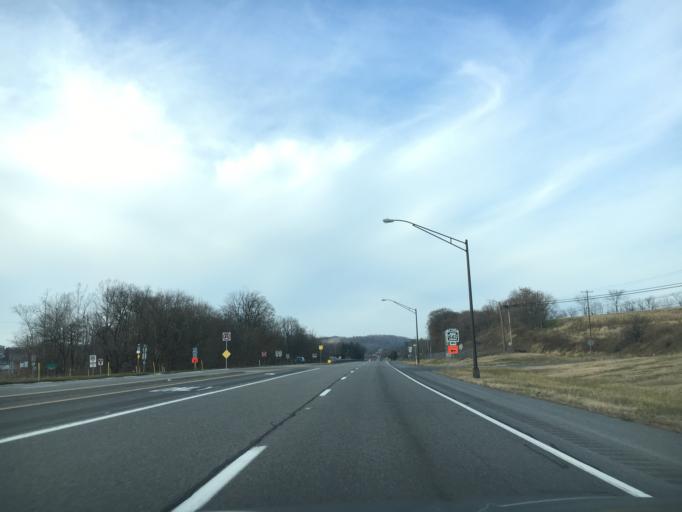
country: US
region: Pennsylvania
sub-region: Montour County
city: Danville
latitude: 40.9858
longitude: -76.6311
